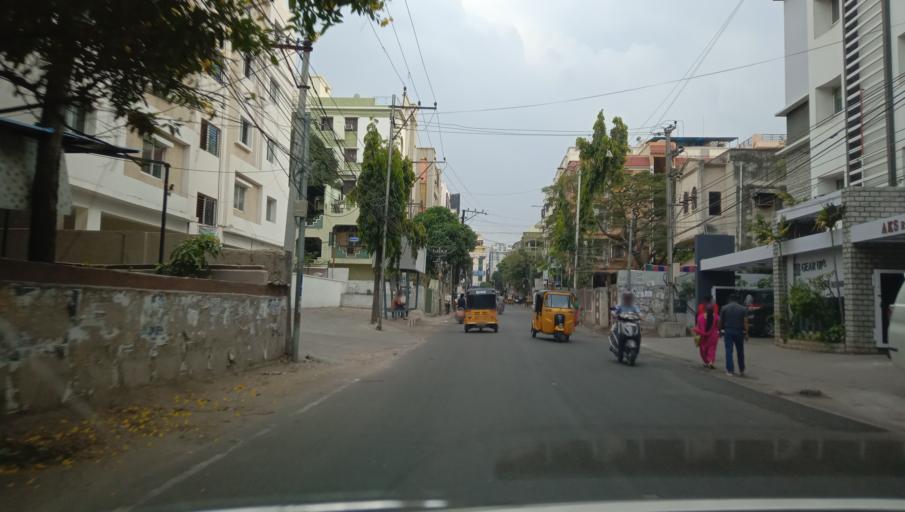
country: IN
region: Telangana
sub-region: Hyderabad
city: Hyderabad
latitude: 17.4029
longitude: 78.4891
